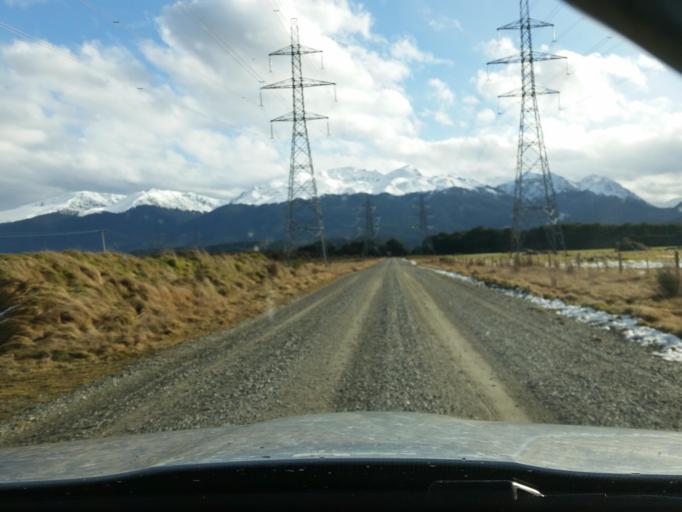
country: NZ
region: Southland
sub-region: Southland District
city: Te Anau
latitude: -45.7770
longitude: 167.5704
